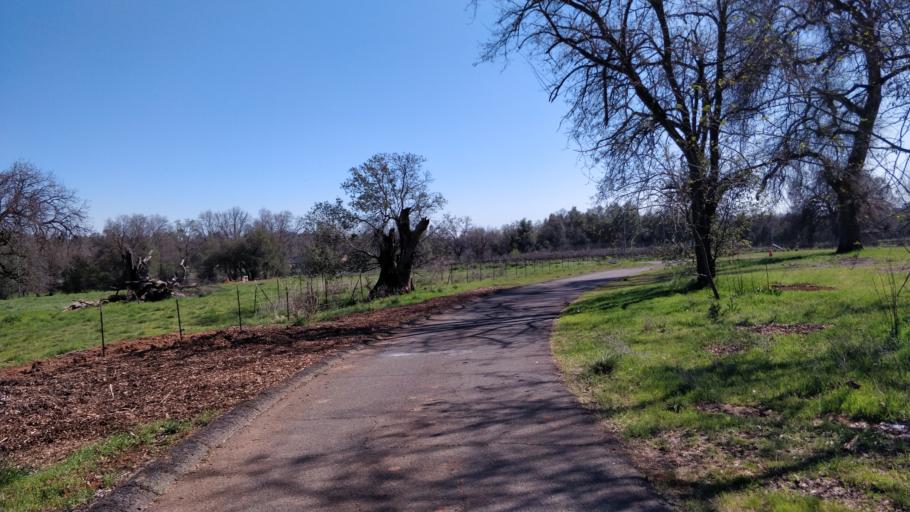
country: US
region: California
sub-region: Shasta County
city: Shasta Lake
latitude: 40.6237
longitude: -122.3150
